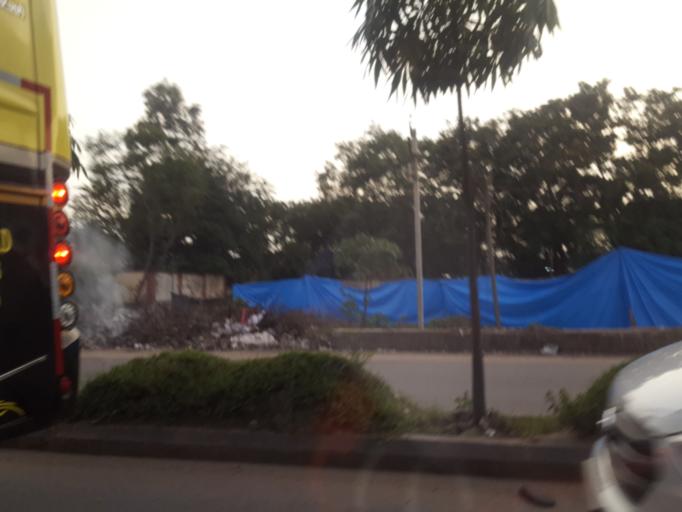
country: IN
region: Telangana
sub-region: Rangareddi
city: Kukatpalli
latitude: 17.5133
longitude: 78.3610
